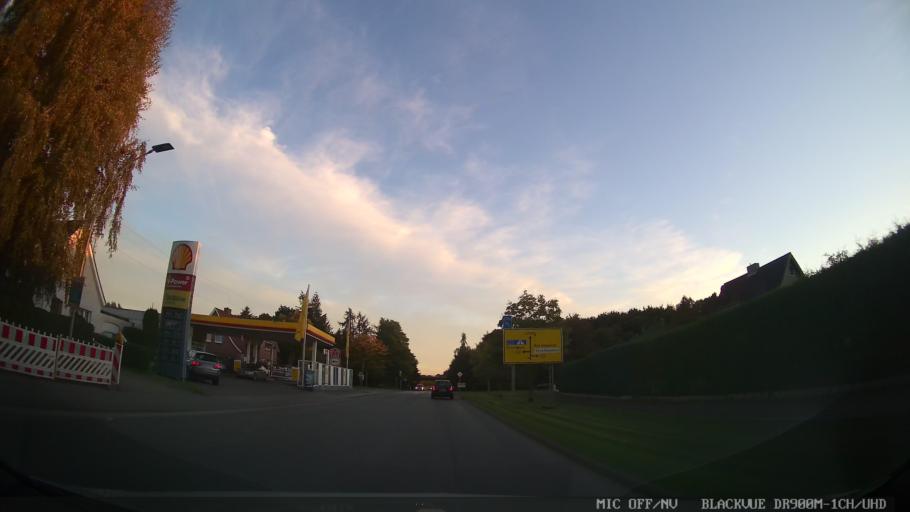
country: DE
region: Schleswig-Holstein
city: Susel
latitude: 54.0436
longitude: 10.6799
